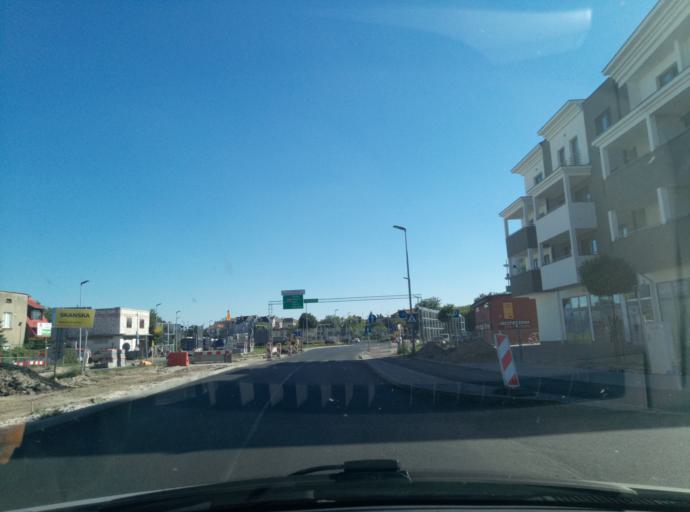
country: PL
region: Kujawsko-Pomorskie
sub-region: Torun
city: Torun
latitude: 53.0264
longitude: 18.5912
